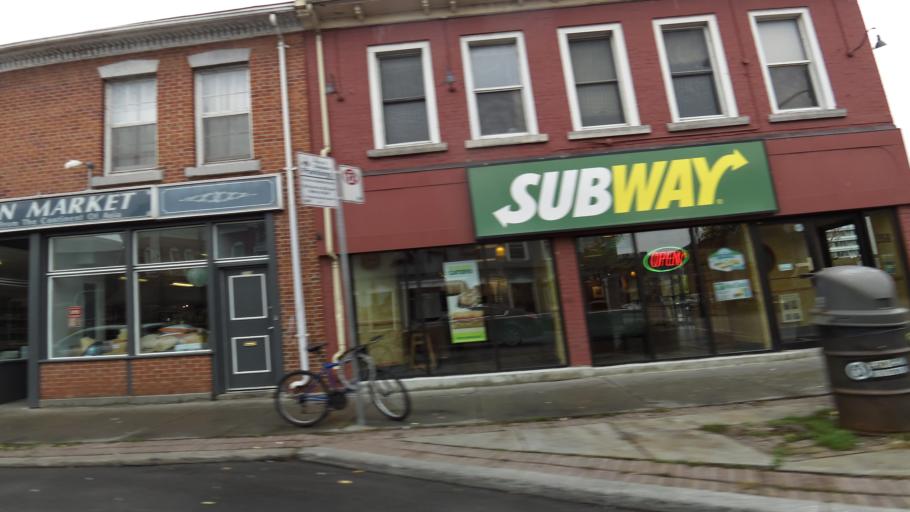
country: CA
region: Ontario
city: Kingston
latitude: 44.2328
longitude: -76.4906
